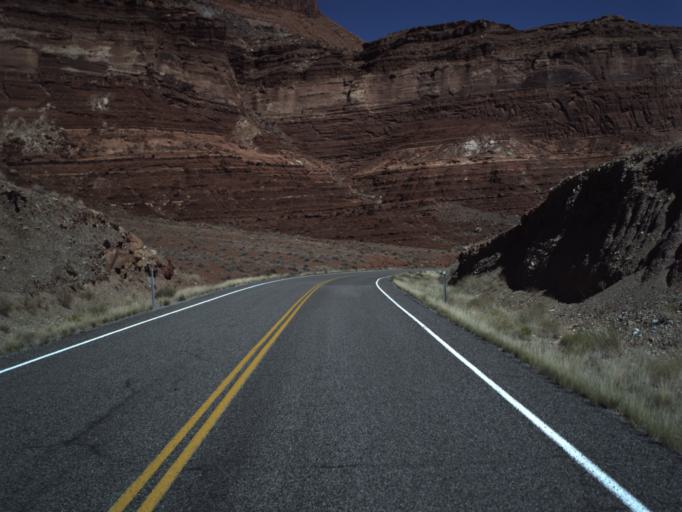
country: US
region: Utah
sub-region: San Juan County
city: Blanding
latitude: 37.9171
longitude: -110.3981
